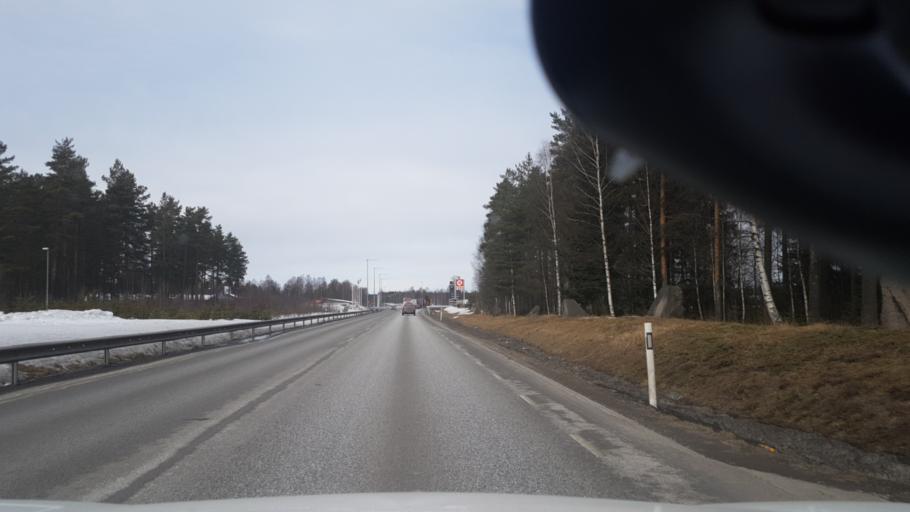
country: SE
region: Vaermland
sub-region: Eda Kommun
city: Charlottenberg
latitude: 59.8760
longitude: 12.2875
